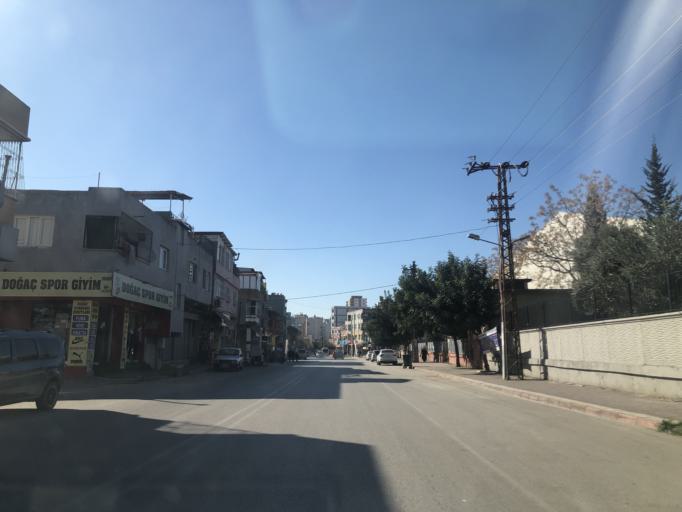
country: TR
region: Adana
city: Yuregir
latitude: 37.0106
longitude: 35.3674
